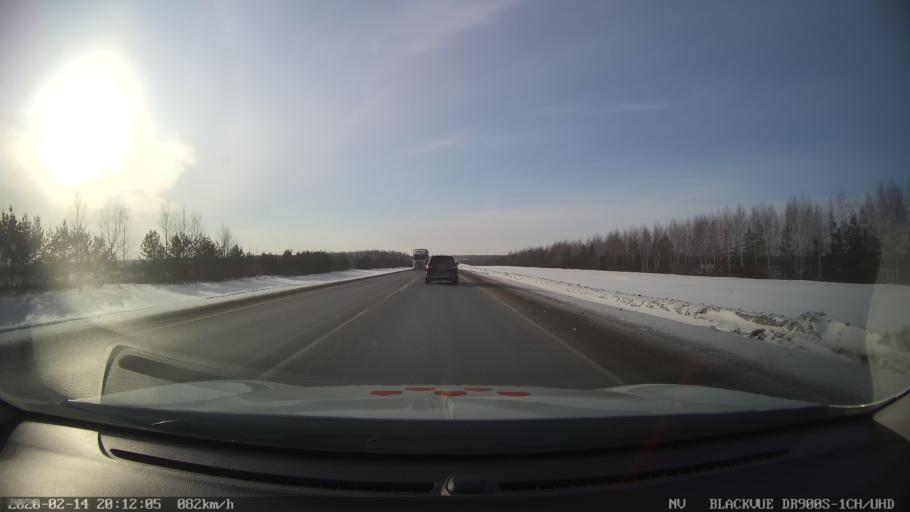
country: RU
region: Tatarstan
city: Verkhniy Uslon
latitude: 55.6699
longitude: 48.8662
